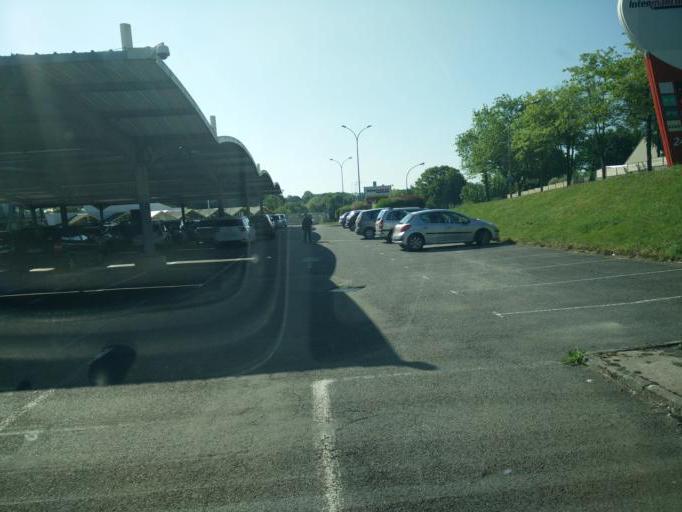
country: FR
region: Brittany
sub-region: Departement du Morbihan
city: Hennebont
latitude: 47.8099
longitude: -3.2633
